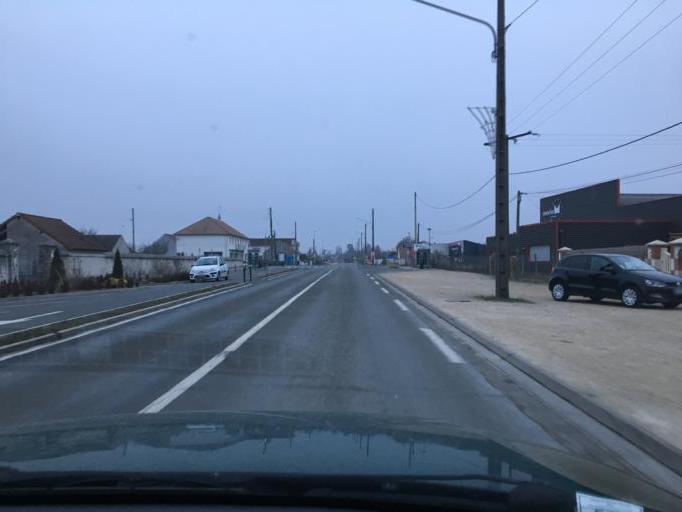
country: FR
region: Centre
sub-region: Departement du Loiret
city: Lailly-en-Val
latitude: 47.7675
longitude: 1.6883
